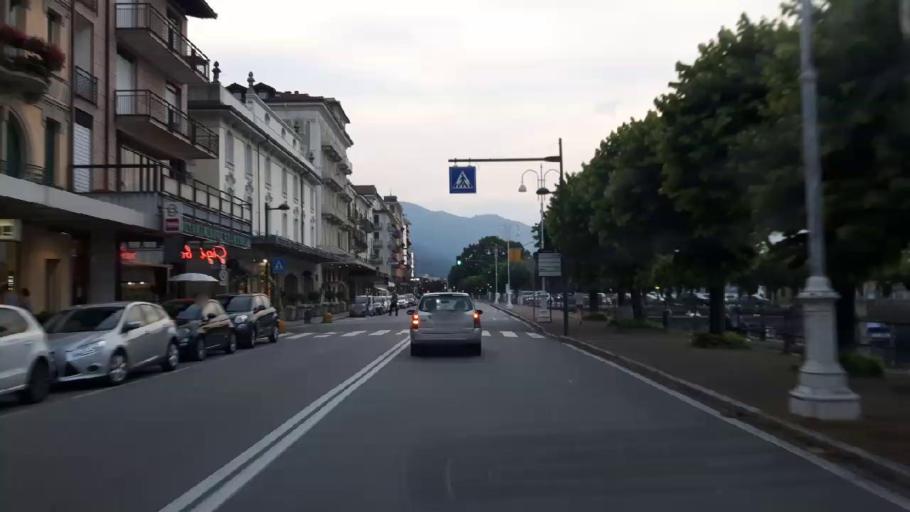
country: IT
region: Piedmont
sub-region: Provincia Verbano-Cusio-Ossola
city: Stresa
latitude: 45.8835
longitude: 8.5425
